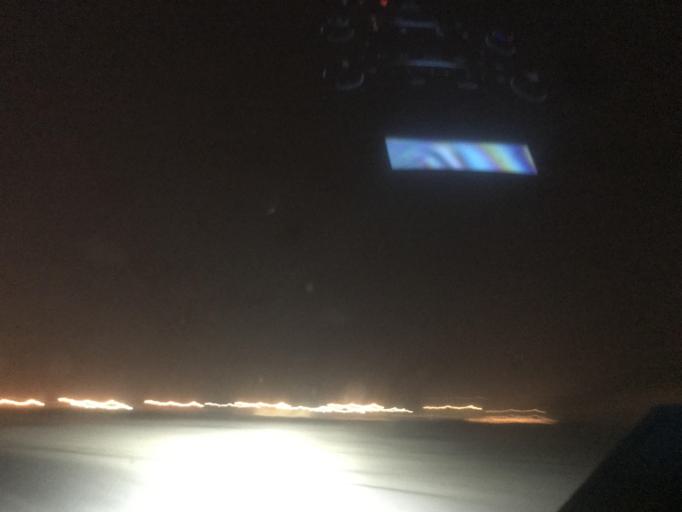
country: SA
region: Ar Riyad
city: Riyadh
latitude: 24.7634
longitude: 46.5865
